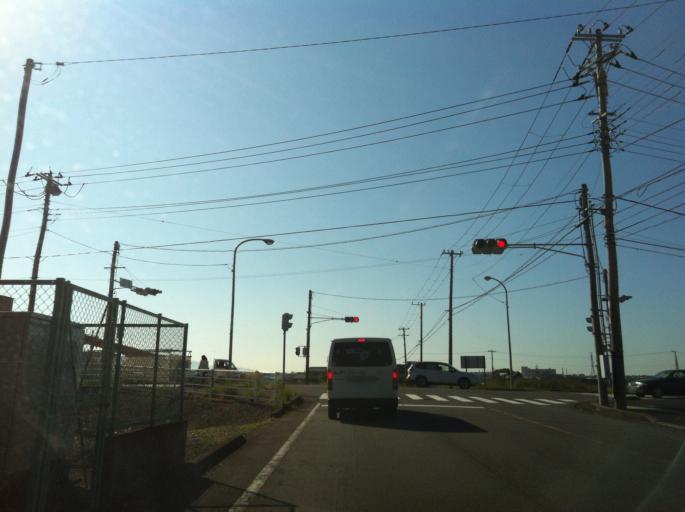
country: JP
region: Shizuoka
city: Fuji
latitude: 35.1454
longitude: 138.7775
